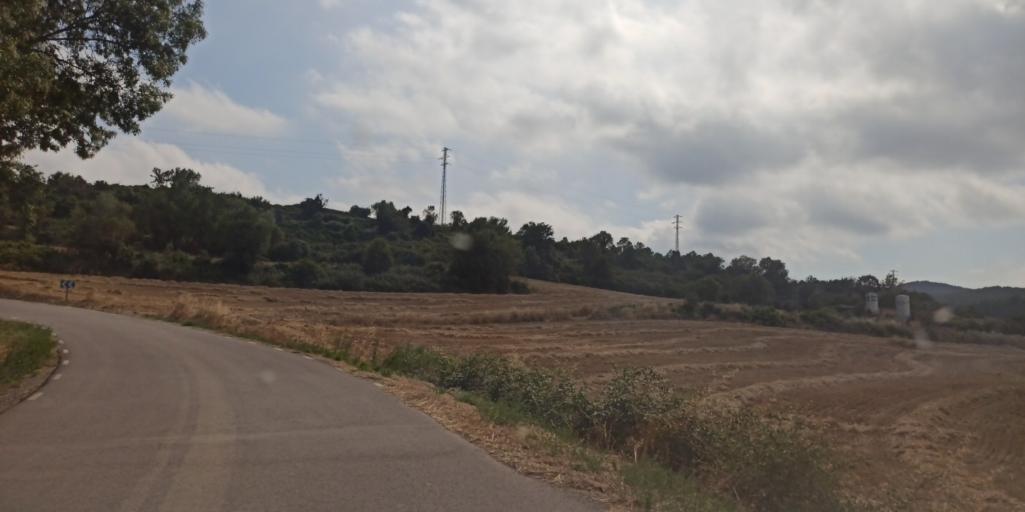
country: ES
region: Catalonia
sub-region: Provincia de Barcelona
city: Sant Joan de Mediona
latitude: 41.4765
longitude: 1.6047
